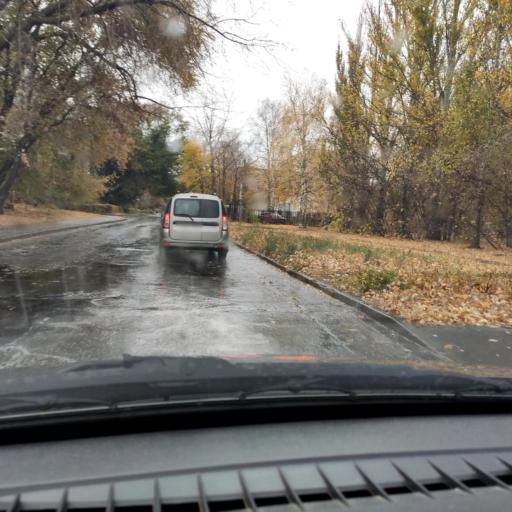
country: RU
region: Samara
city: Tol'yatti
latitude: 53.5325
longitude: 49.2628
